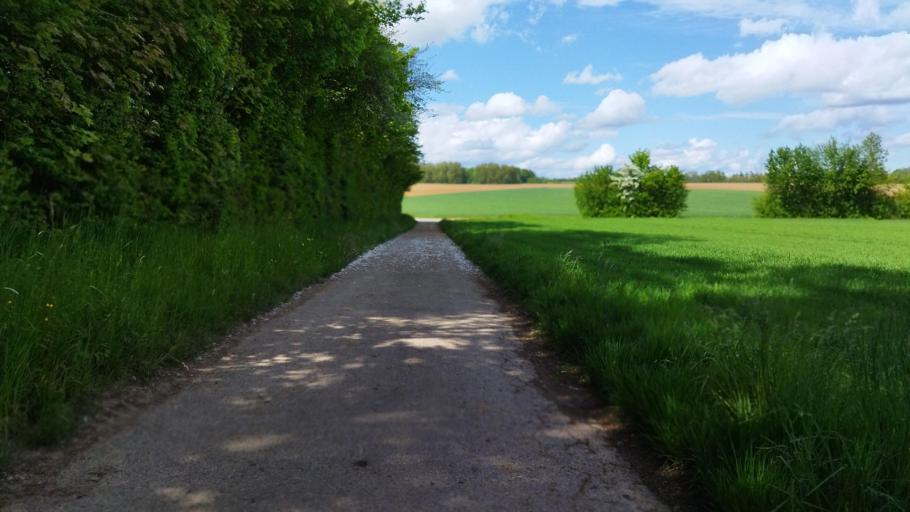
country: DE
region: Baden-Wuerttemberg
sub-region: Regierungsbezirk Stuttgart
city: Bad Rappenau
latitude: 49.2209
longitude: 9.0905
